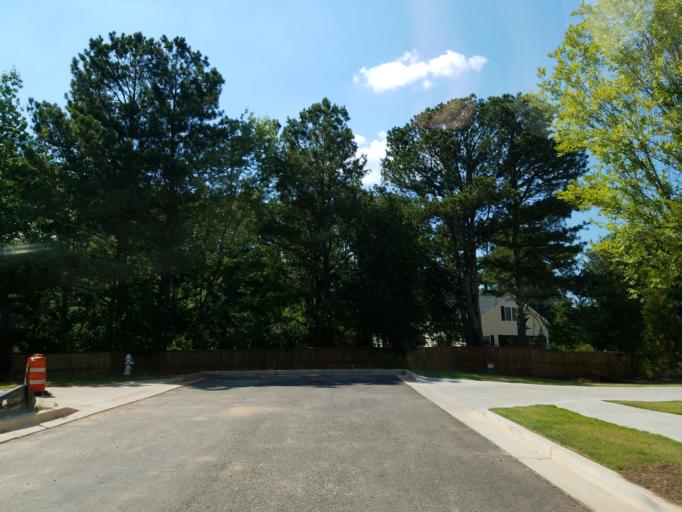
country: US
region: Georgia
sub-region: Fulton County
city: Roswell
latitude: 34.0866
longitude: -84.3580
